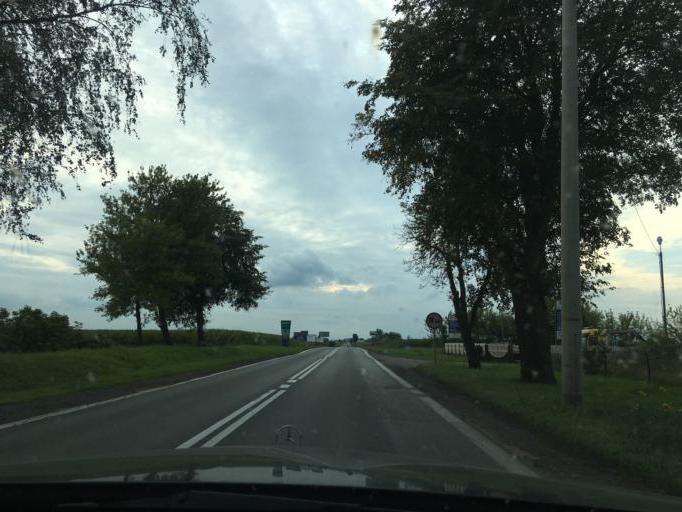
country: PL
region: Podlasie
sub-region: Powiat grajewski
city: Grajewo
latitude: 53.6392
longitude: 22.4373
